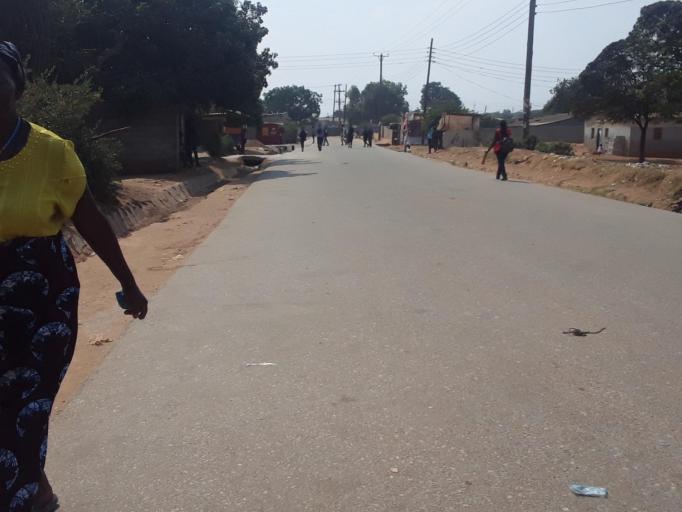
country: ZM
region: Lusaka
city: Lusaka
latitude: -15.3563
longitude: 28.2957
